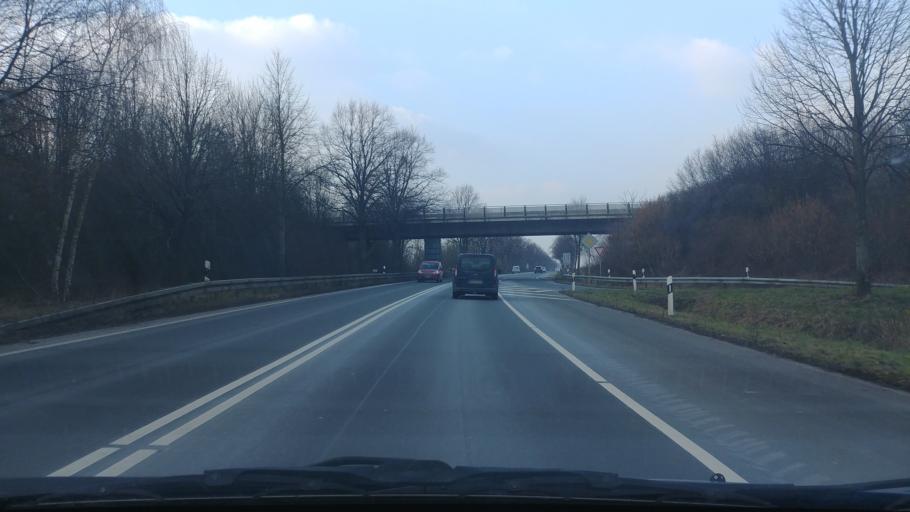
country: DE
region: Lower Saxony
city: Pattensen
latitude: 52.2771
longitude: 9.7597
